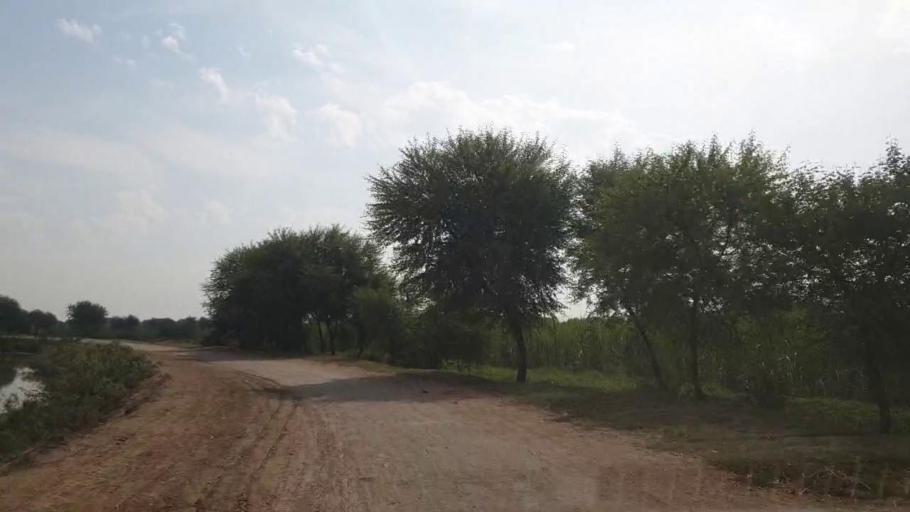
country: PK
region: Sindh
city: Rajo Khanani
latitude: 24.9570
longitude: 69.0102
